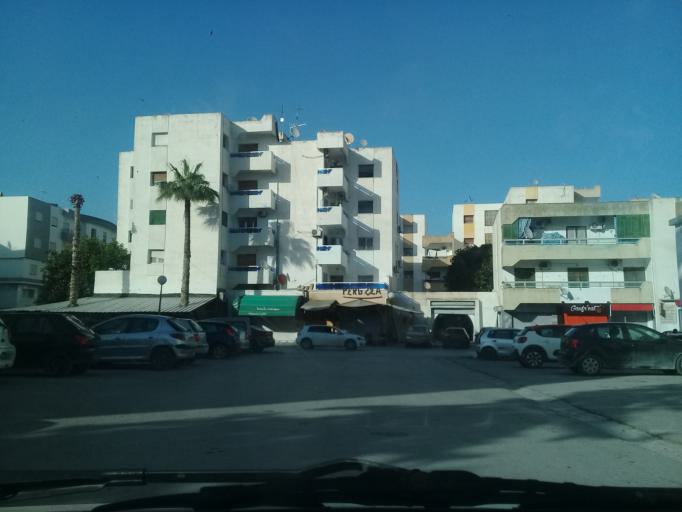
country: TN
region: Ariana
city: Ariana
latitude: 36.8376
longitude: 10.1920
